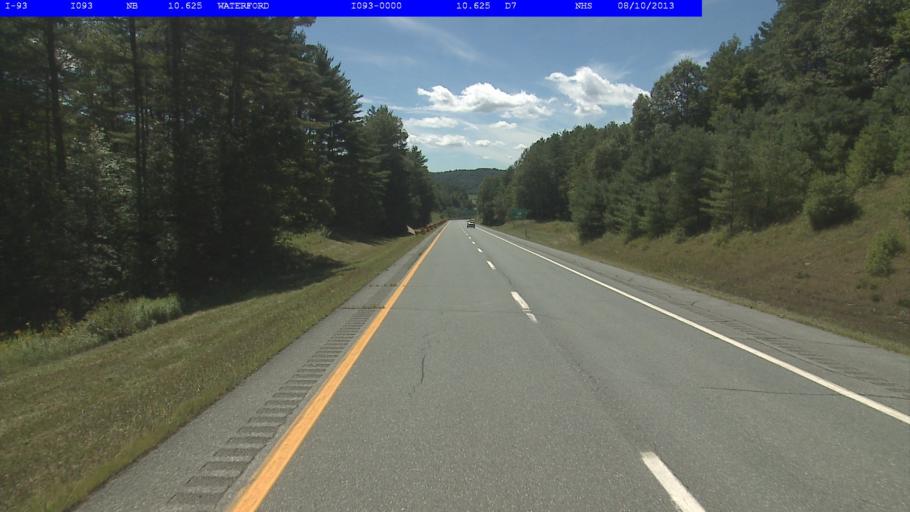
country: US
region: Vermont
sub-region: Caledonia County
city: Saint Johnsbury
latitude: 44.4024
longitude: -72.0078
